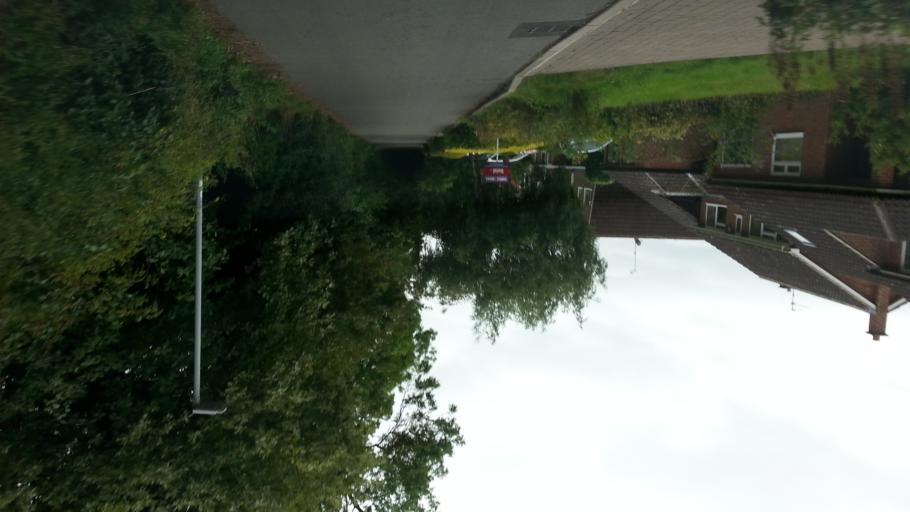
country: GB
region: England
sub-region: Nottinghamshire
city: Southwell
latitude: 53.0822
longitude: -0.9628
